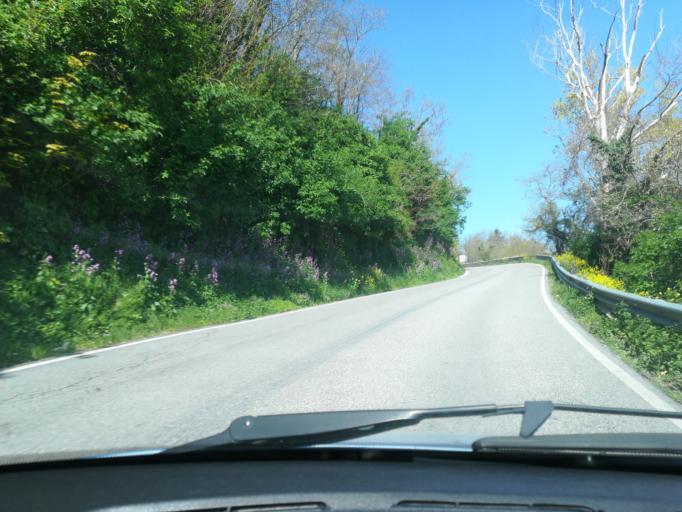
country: IT
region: The Marches
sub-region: Provincia di Macerata
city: Cingoli
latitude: 43.3766
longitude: 13.2203
